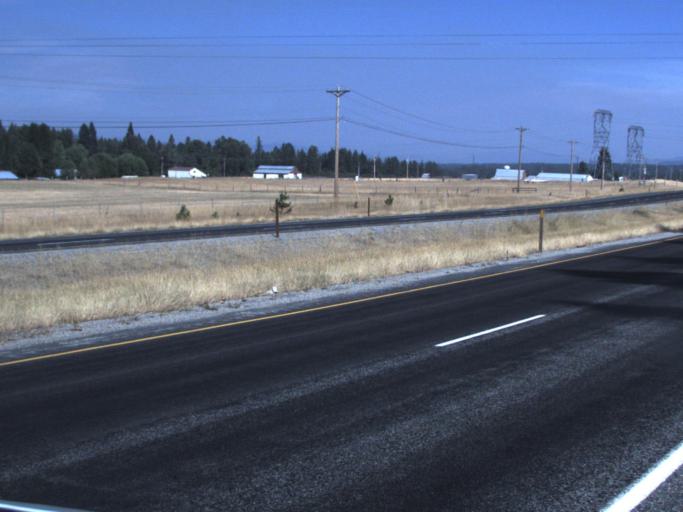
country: US
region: Washington
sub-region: Spokane County
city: Deer Park
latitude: 48.0966
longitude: -117.2889
